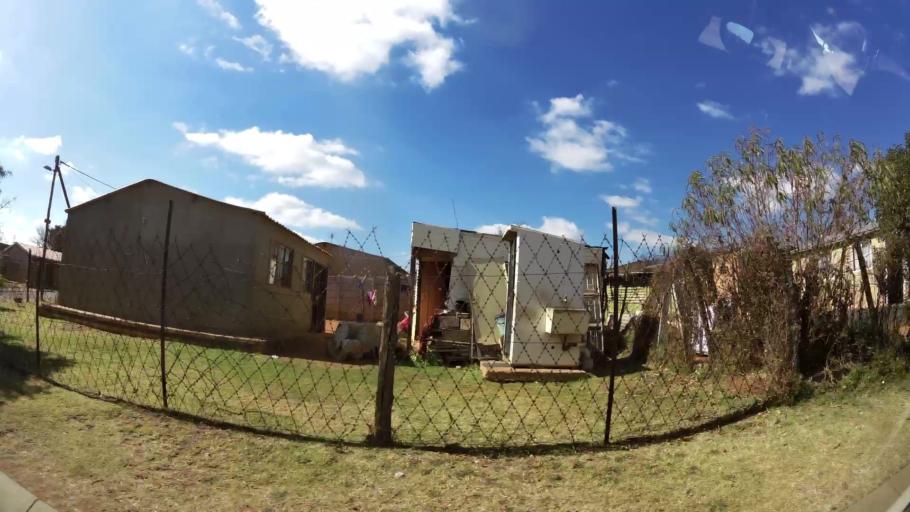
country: ZA
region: Gauteng
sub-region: West Rand District Municipality
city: Krugersdorp
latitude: -26.1427
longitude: 27.7874
